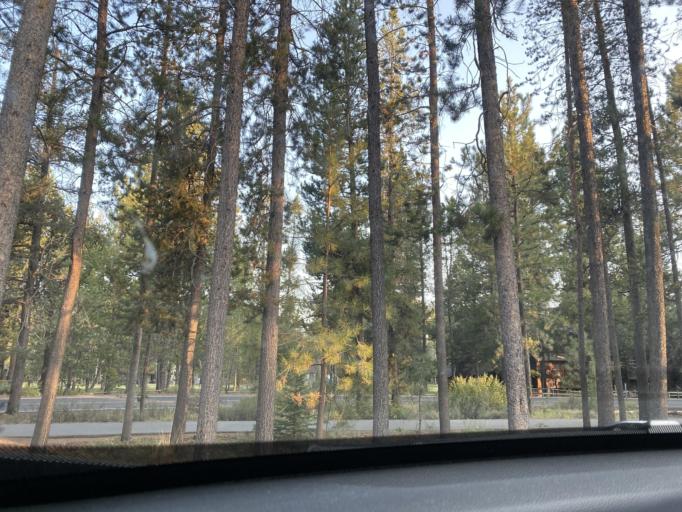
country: US
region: Oregon
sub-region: Deschutes County
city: Sunriver
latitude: 43.8746
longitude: -121.4374
